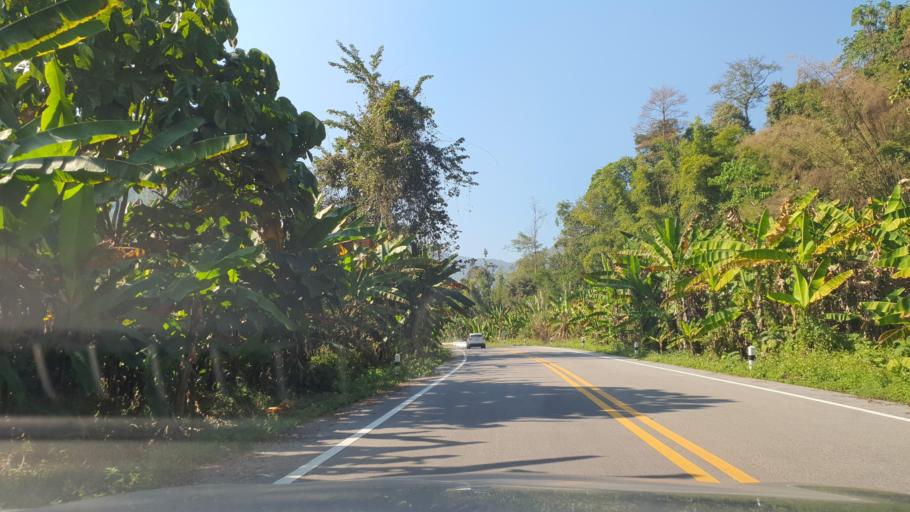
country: TH
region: Chiang Rai
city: Mae Lao
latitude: 19.8683
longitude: 99.6344
